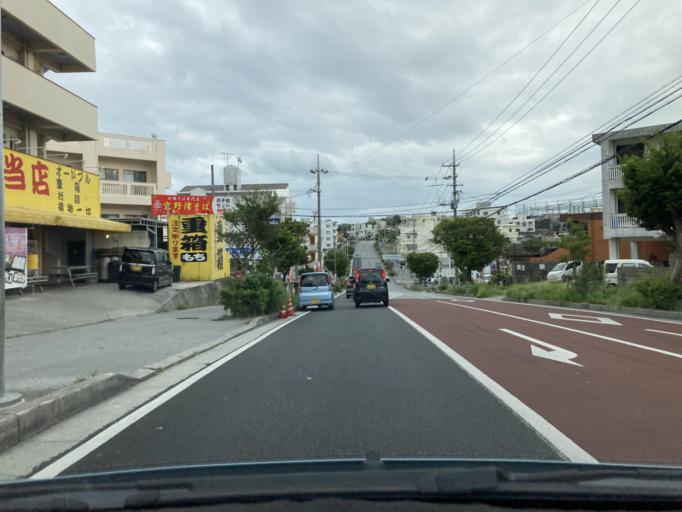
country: JP
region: Okinawa
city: Ginowan
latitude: 26.2538
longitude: 127.7569
